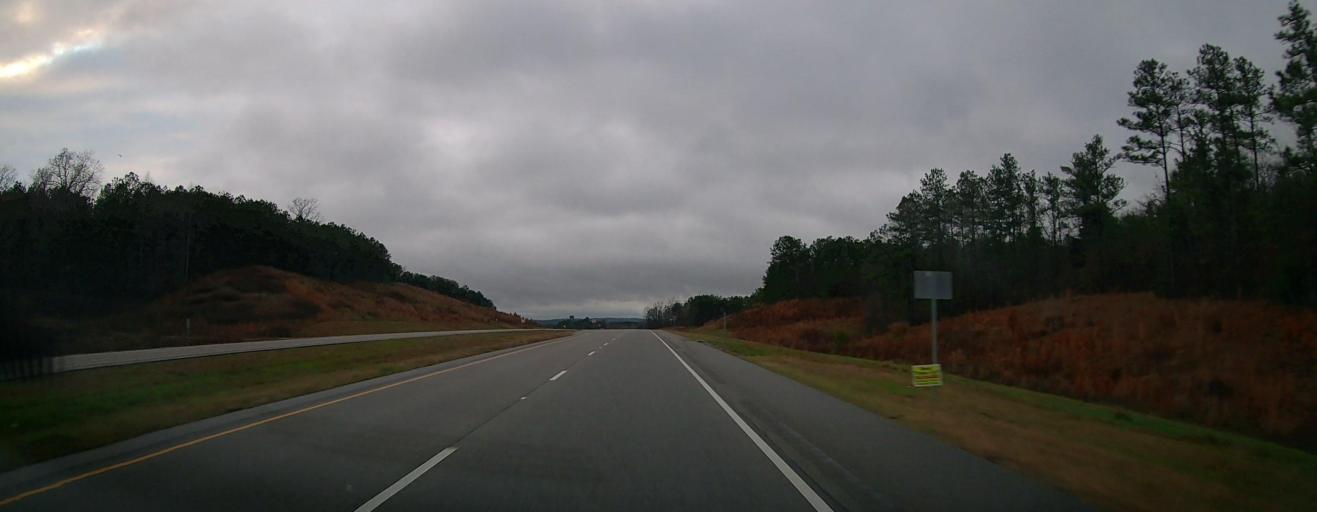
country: US
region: Alabama
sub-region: Bibb County
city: Centreville
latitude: 32.9525
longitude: -87.1101
